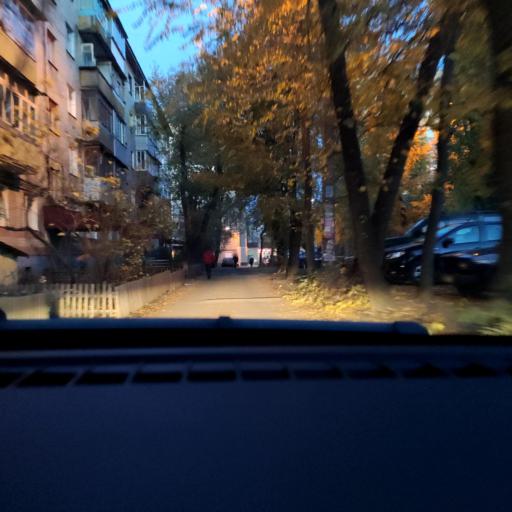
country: RU
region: Voronezj
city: Voronezh
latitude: 51.6829
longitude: 39.2647
